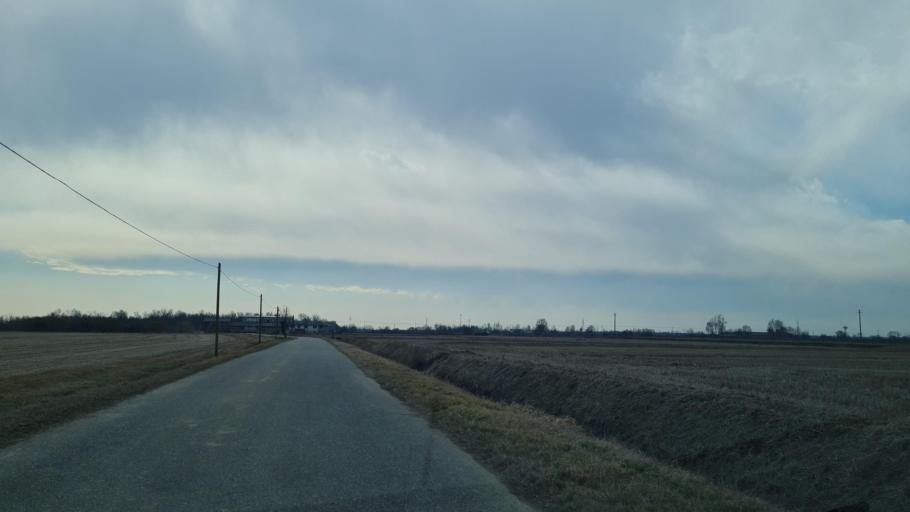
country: IT
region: Piedmont
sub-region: Provincia di Vercelli
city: Buronzo
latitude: 45.4633
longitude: 8.2524
